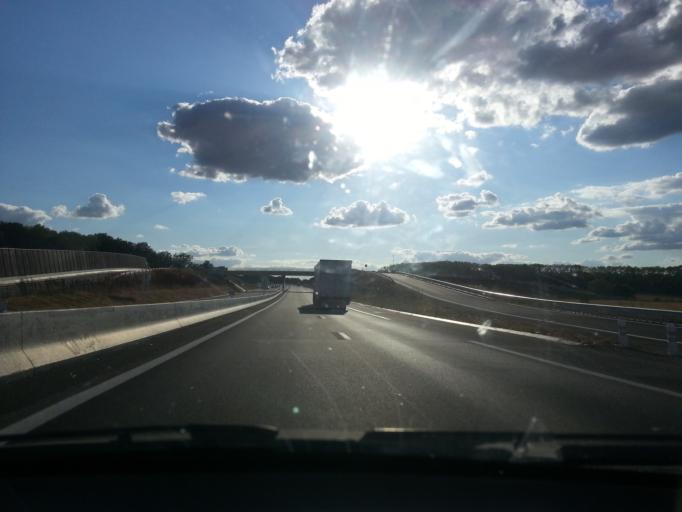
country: FR
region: Bourgogne
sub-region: Departement de Saone-et-Loire
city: Saint-Remy
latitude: 46.7555
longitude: 4.8186
